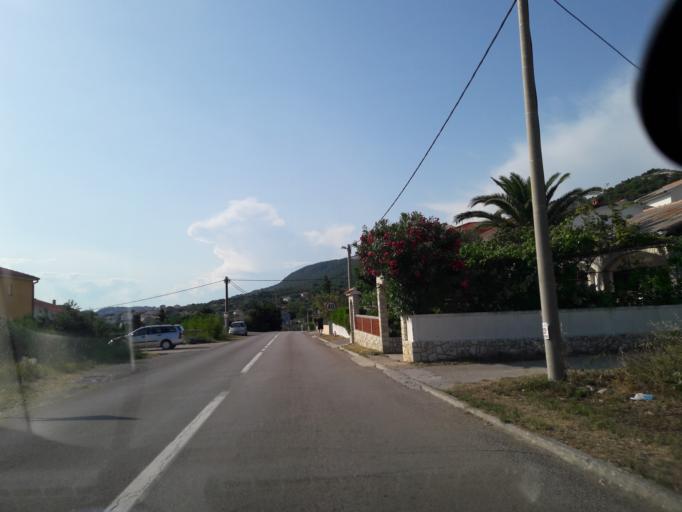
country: HR
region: Primorsko-Goranska
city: Banjol
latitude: 44.7381
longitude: 14.8022
